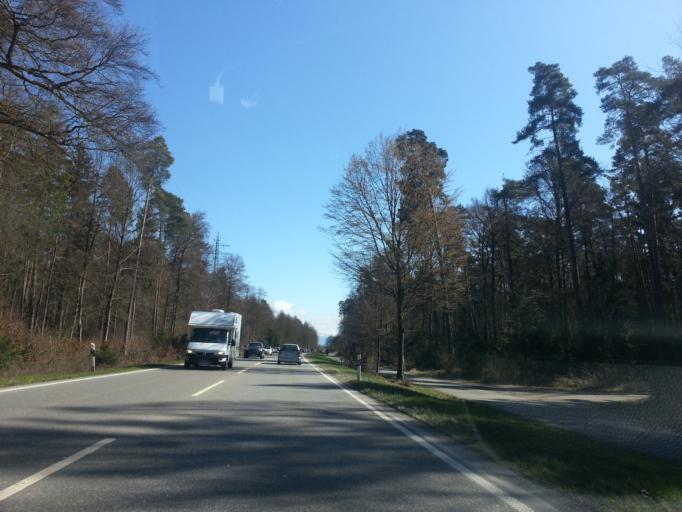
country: DE
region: Baden-Wuerttemberg
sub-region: Tuebingen Region
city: Eriskirch
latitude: 47.6215
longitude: 9.5590
